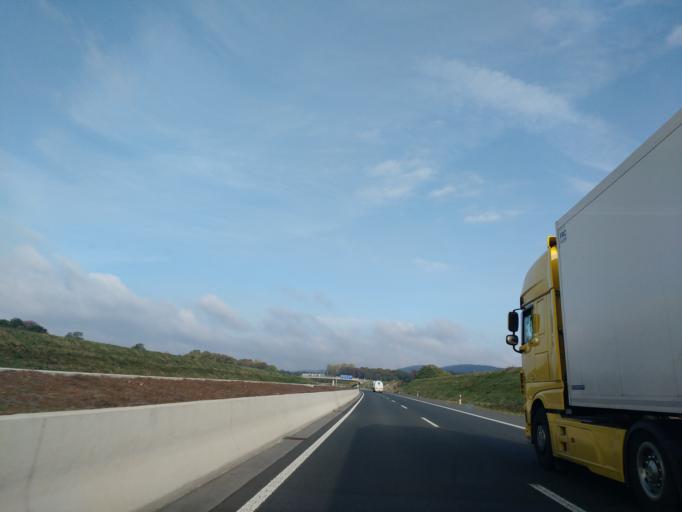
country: DE
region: North Rhine-Westphalia
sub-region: Regierungsbezirk Detmold
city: Steinhagen
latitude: 51.9987
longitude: 8.4419
